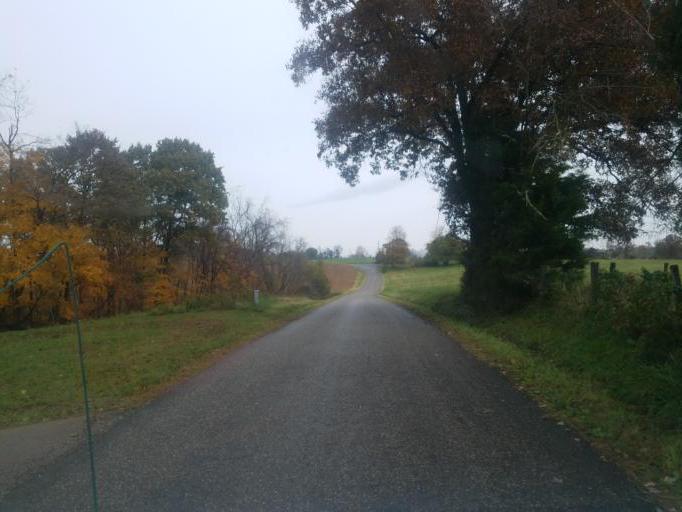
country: US
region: Ohio
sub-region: Washington County
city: Beverly
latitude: 39.5492
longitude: -81.7035
